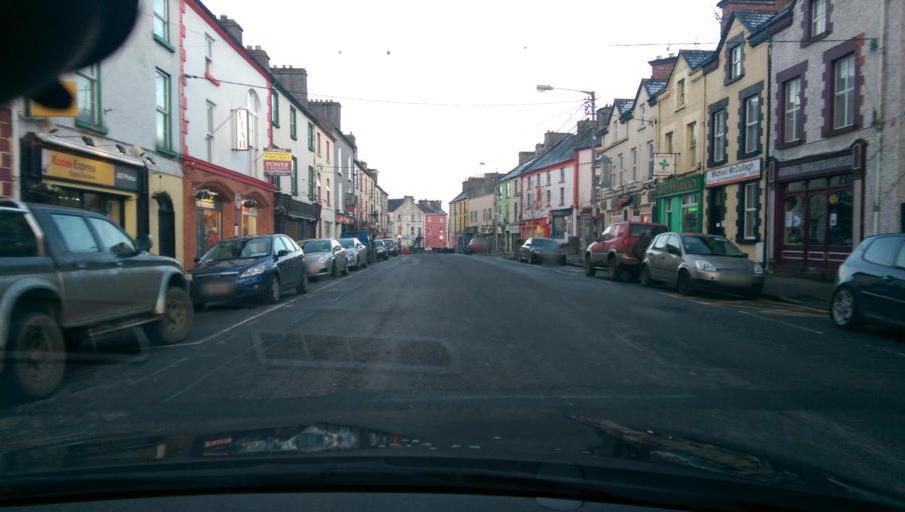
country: IE
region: Connaught
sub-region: County Galway
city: Ballinasloe
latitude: 53.3306
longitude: -8.2234
